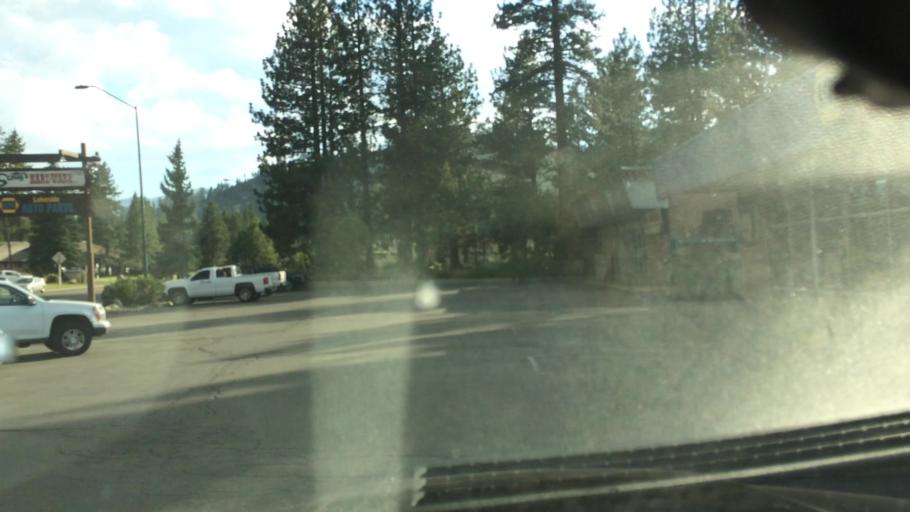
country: US
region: California
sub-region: El Dorado County
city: South Lake Tahoe
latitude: 38.9128
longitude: -120.0070
